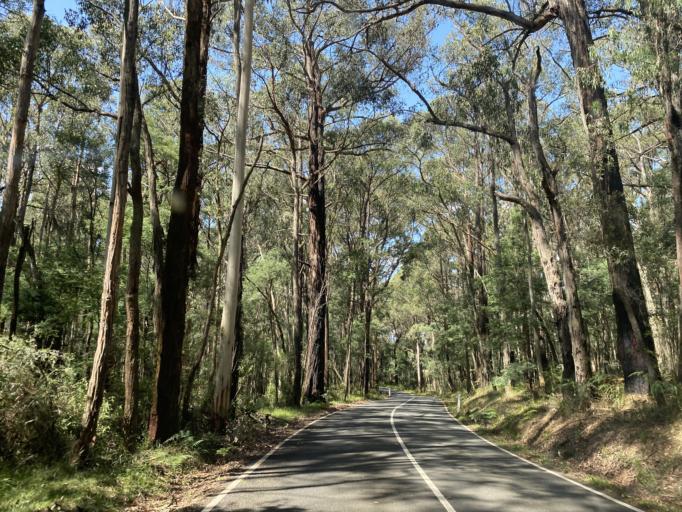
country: AU
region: Victoria
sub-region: Cardinia
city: Gembrook
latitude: -37.9839
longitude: 145.6025
